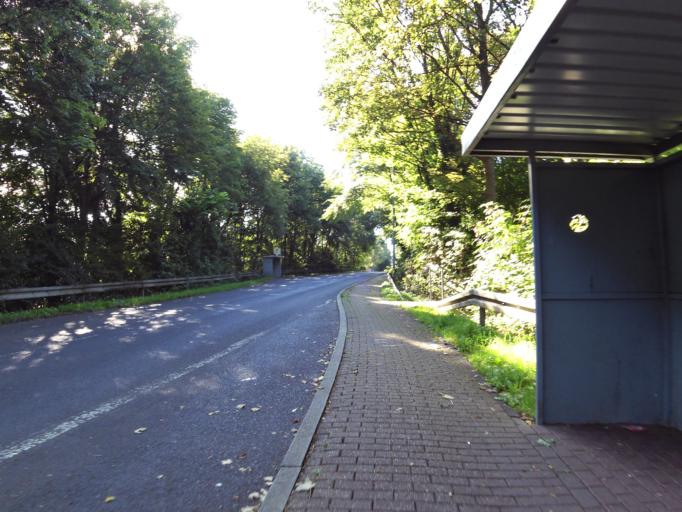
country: DE
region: North Rhine-Westphalia
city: Siersdorf
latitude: 50.8644
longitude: 6.2153
